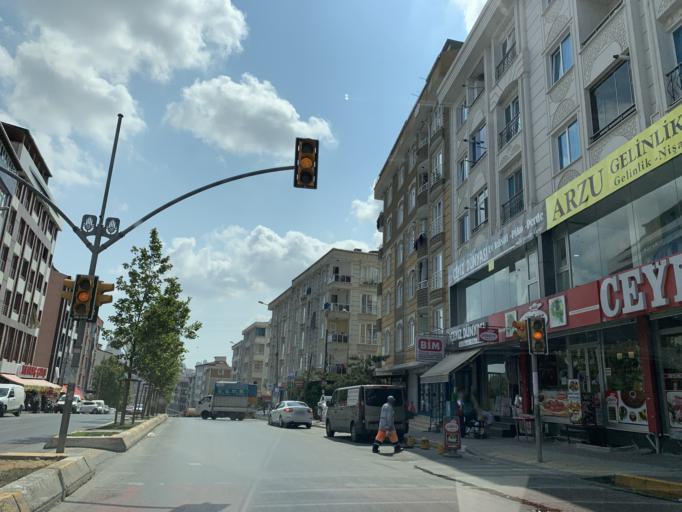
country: TR
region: Istanbul
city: Esenyurt
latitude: 41.0444
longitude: 28.6642
